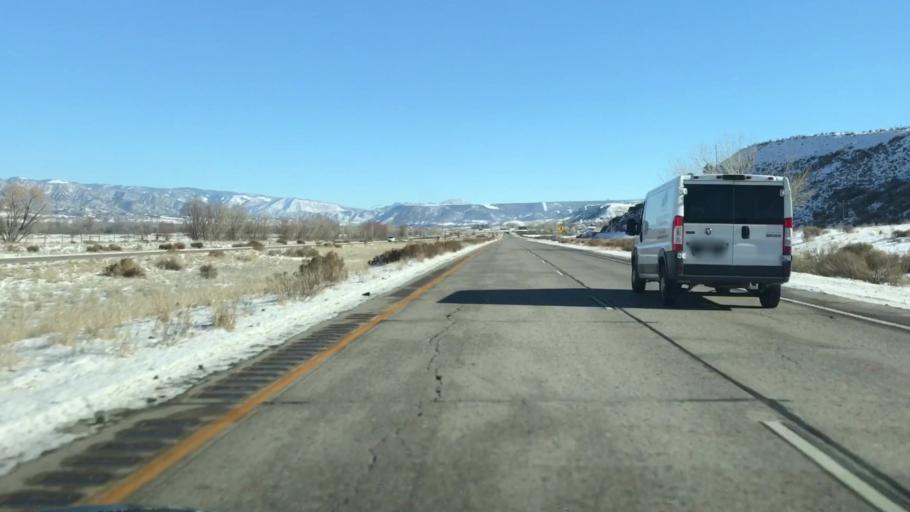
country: US
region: Colorado
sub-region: Garfield County
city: Silt
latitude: 39.5318
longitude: -107.7123
